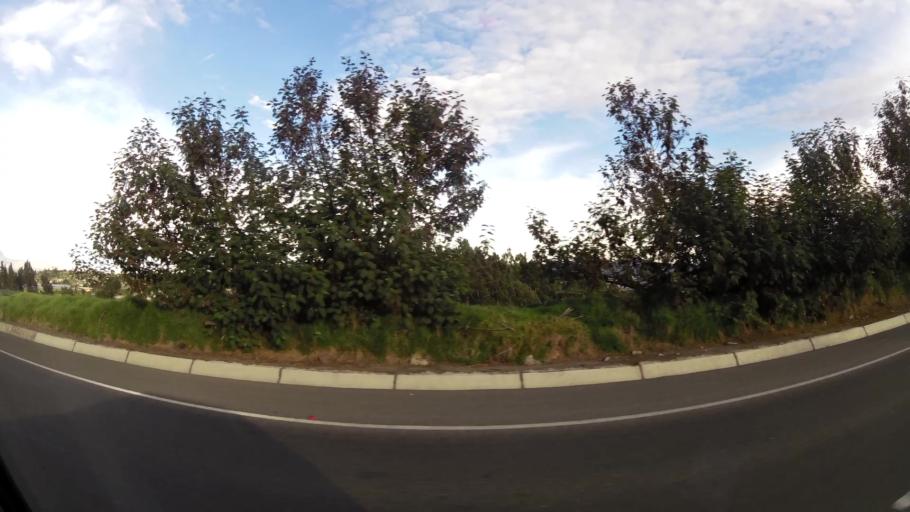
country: EC
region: Cotopaxi
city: Saquisili
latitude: -0.8565
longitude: -78.6214
